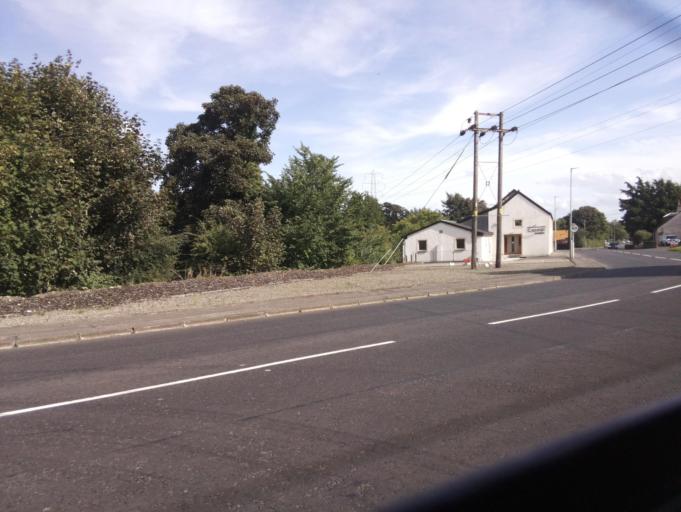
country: GB
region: Scotland
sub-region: Falkirk
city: Larbert
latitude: 56.0154
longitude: -3.8304
